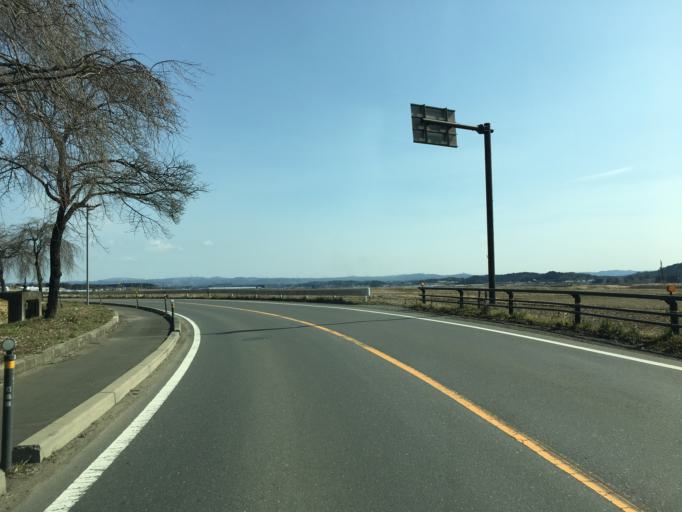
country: JP
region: Fukushima
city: Ishikawa
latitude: 37.1275
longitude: 140.3035
